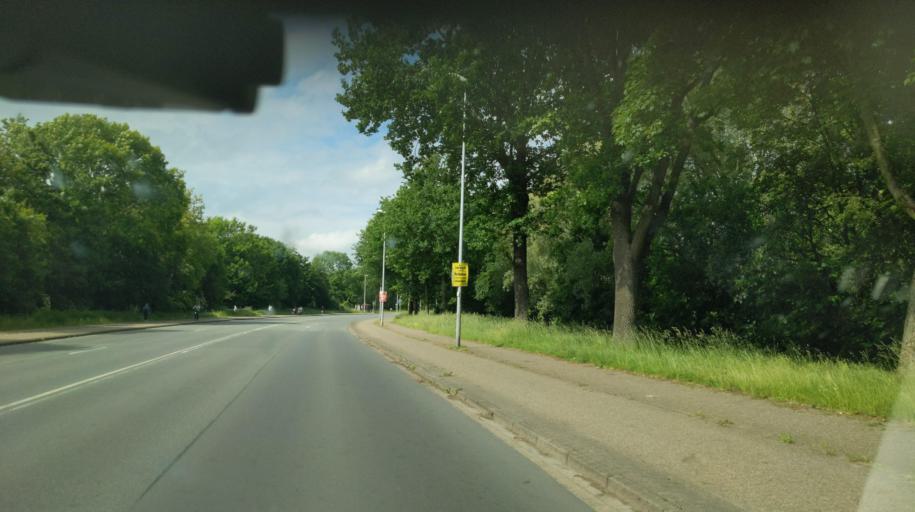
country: DE
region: Lower Saxony
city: Nordenham
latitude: 53.4990
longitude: 8.4891
